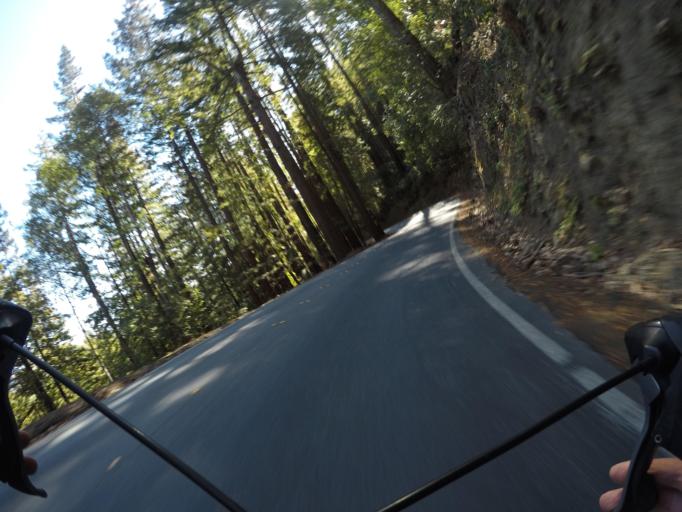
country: US
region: California
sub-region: San Mateo County
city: Portola Valley
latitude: 37.2997
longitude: -122.2698
